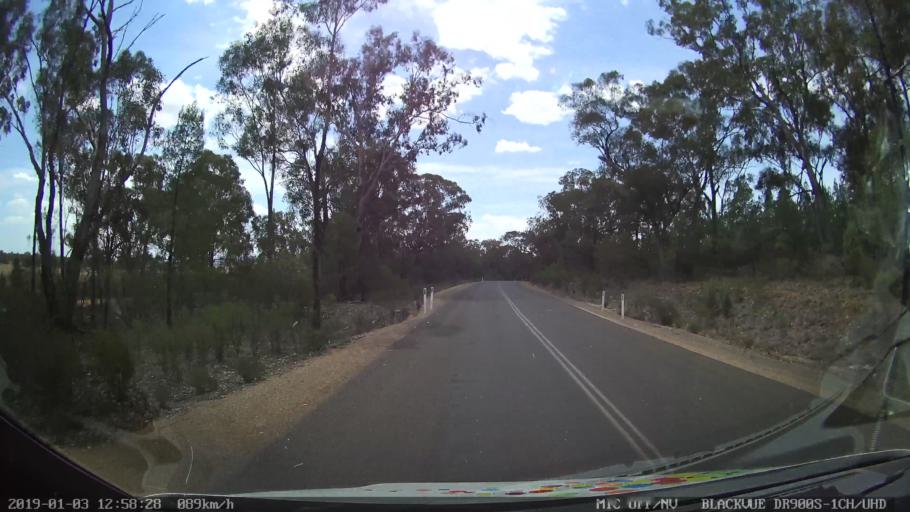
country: AU
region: New South Wales
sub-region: Cabonne
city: Canowindra
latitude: -33.6417
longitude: 148.3755
